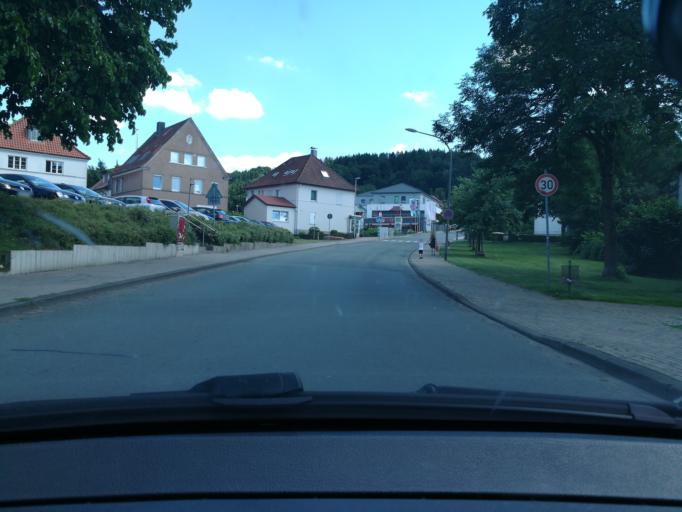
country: DE
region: North Rhine-Westphalia
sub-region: Regierungsbezirk Detmold
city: Oerlinghausen
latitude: 51.9617
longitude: 8.6626
